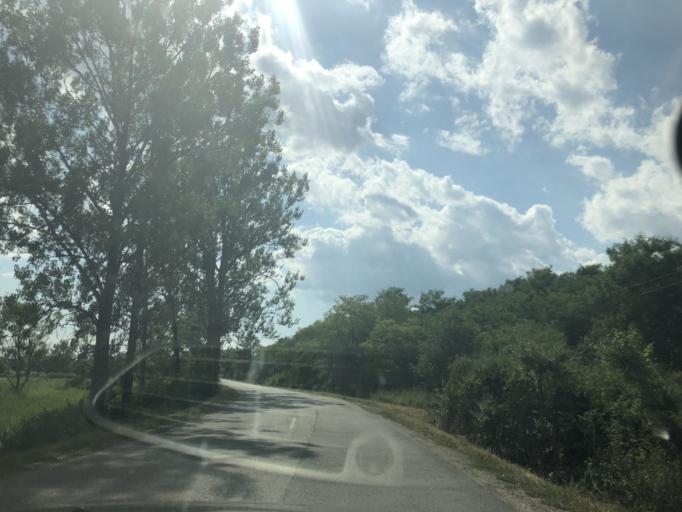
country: HU
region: Borsod-Abauj-Zemplen
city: Szendro
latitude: 48.4571
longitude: 20.7876
